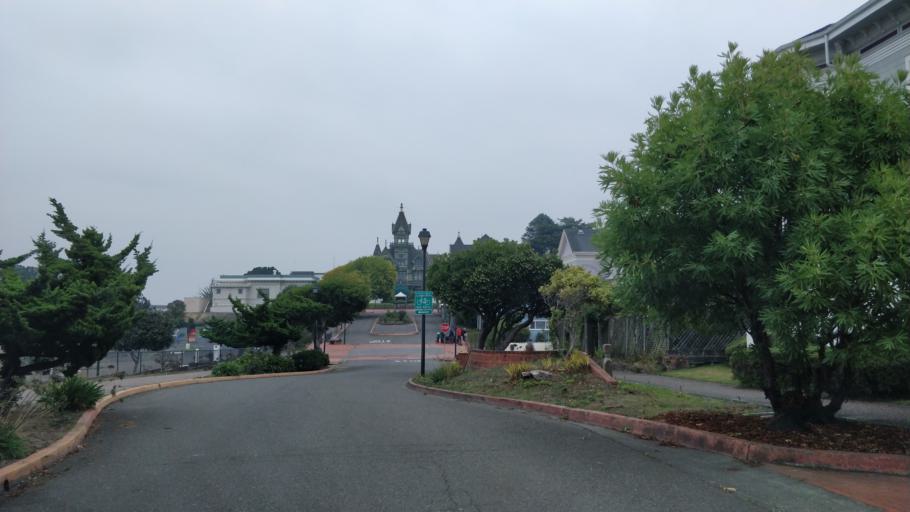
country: US
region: California
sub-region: Humboldt County
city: Eureka
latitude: 40.8051
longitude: -124.1612
